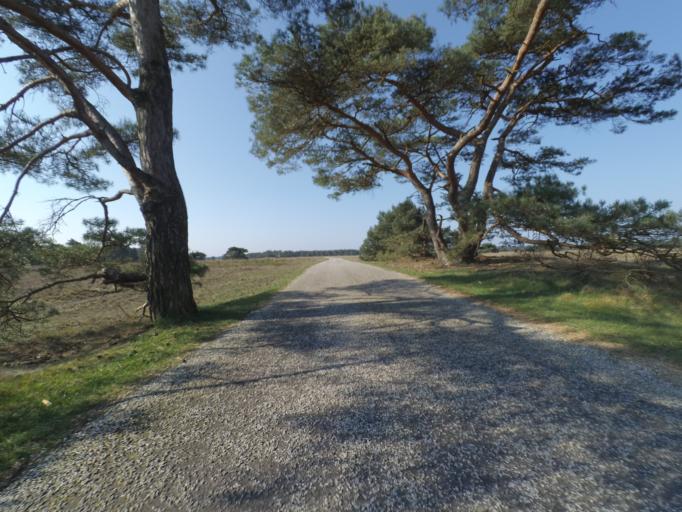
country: NL
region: Gelderland
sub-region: Gemeente Ede
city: Otterlo
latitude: 52.1158
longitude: 5.8092
